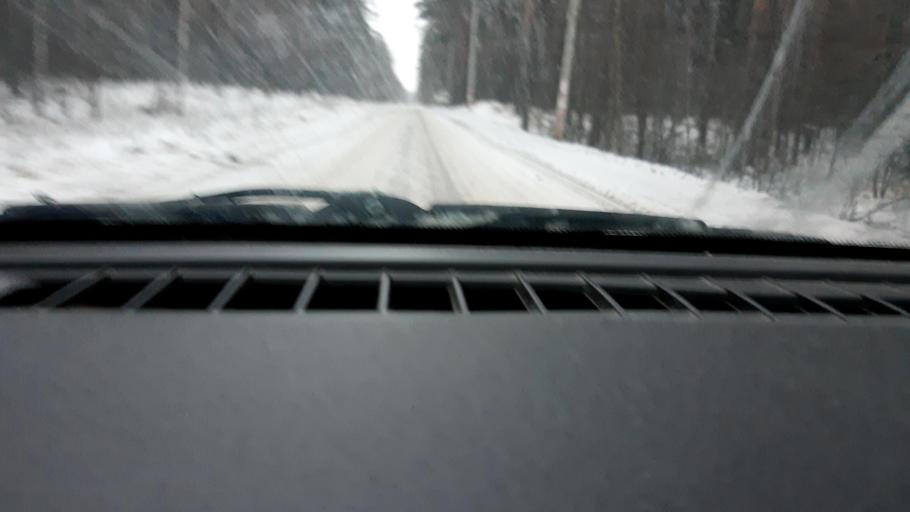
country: RU
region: Nizjnij Novgorod
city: Afonino
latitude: 56.1744
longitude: 44.0847
